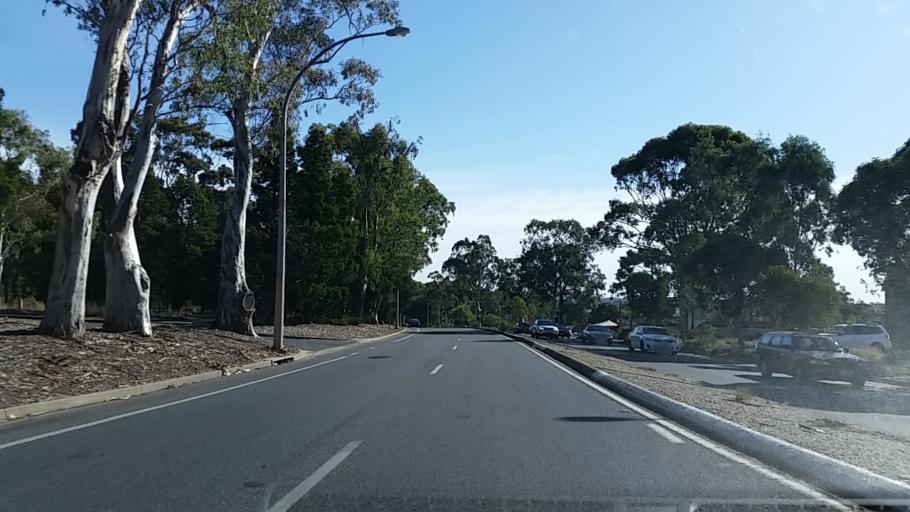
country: AU
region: South Australia
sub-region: Campbelltown
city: Athelstone
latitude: -34.8530
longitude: 138.7000
